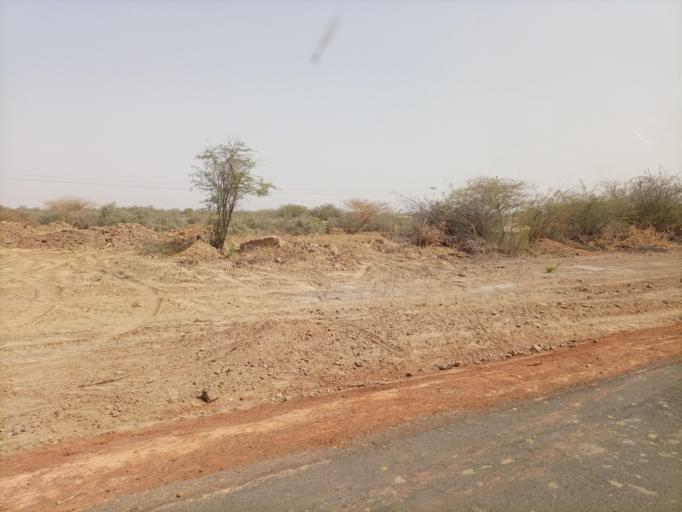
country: SN
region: Fatick
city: Foundiougne
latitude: 14.1592
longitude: -16.4680
